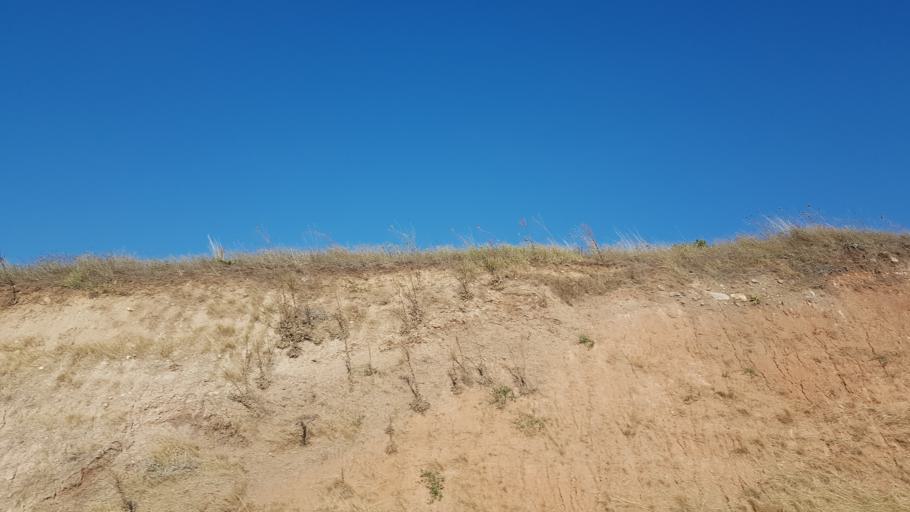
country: TR
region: Balikesir
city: Ertugrul
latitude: 39.5856
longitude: 27.6975
